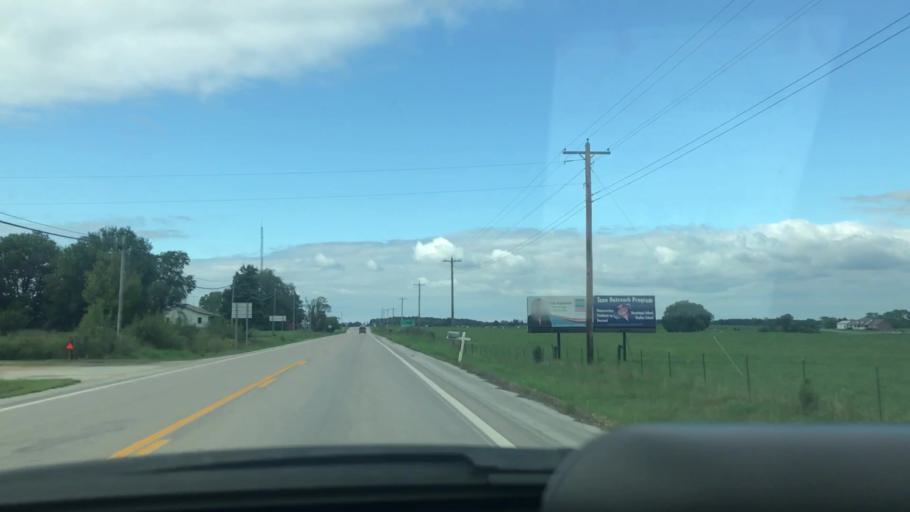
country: US
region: Missouri
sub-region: Hickory County
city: Hermitage
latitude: 37.9430
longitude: -93.2079
